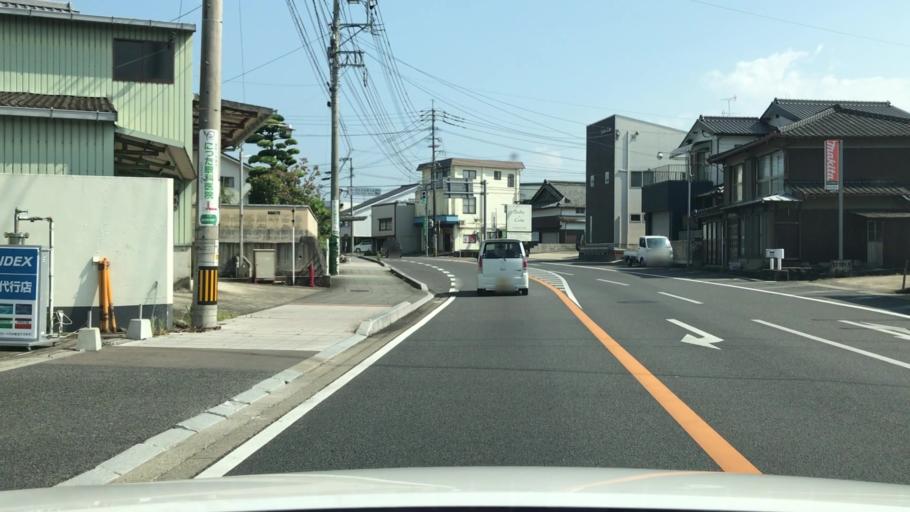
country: JP
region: Saga Prefecture
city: Kashima
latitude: 33.1273
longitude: 130.0593
